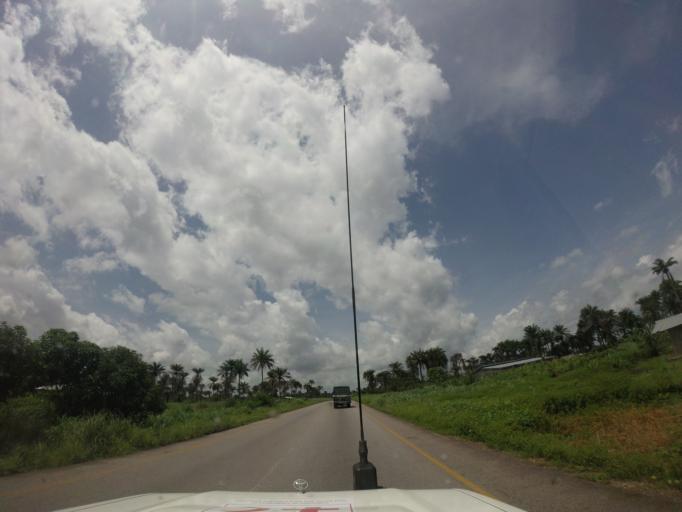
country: SL
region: Northern Province
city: Rokupr
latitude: 8.4823
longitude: -12.4324
